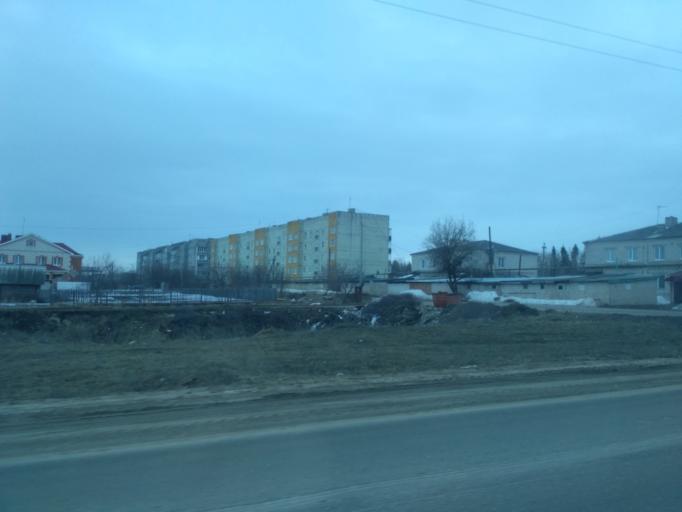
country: RU
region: Nizjnij Novgorod
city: Perevoz
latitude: 55.5989
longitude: 44.5611
